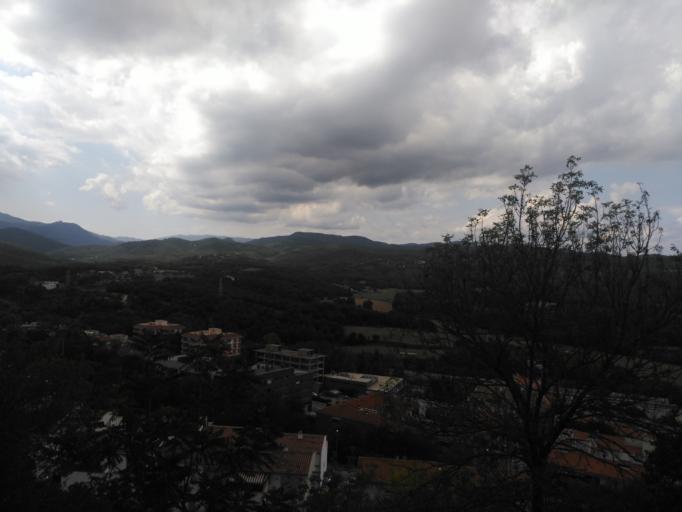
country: ES
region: Catalonia
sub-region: Provincia de Girona
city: Hostalric
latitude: 41.7447
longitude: 2.6331
